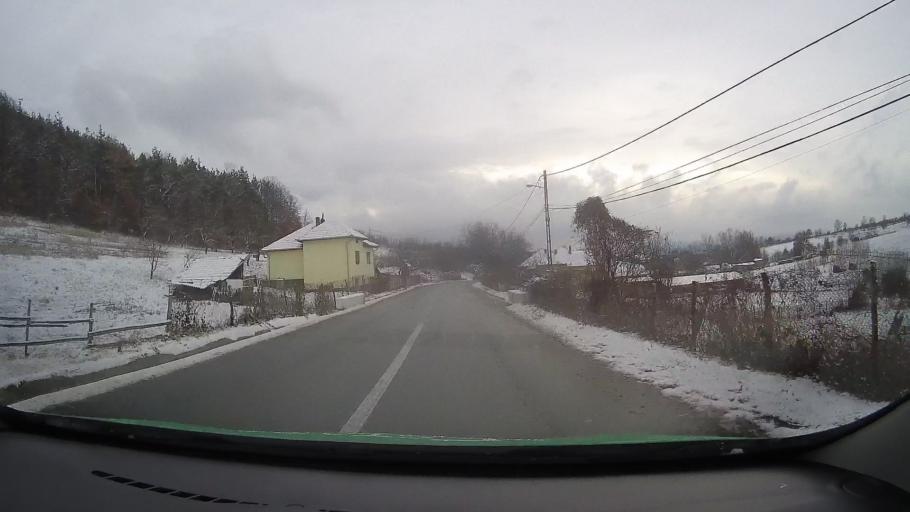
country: RO
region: Hunedoara
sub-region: Oras Hateg
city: Hateg
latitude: 45.6257
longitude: 22.9358
